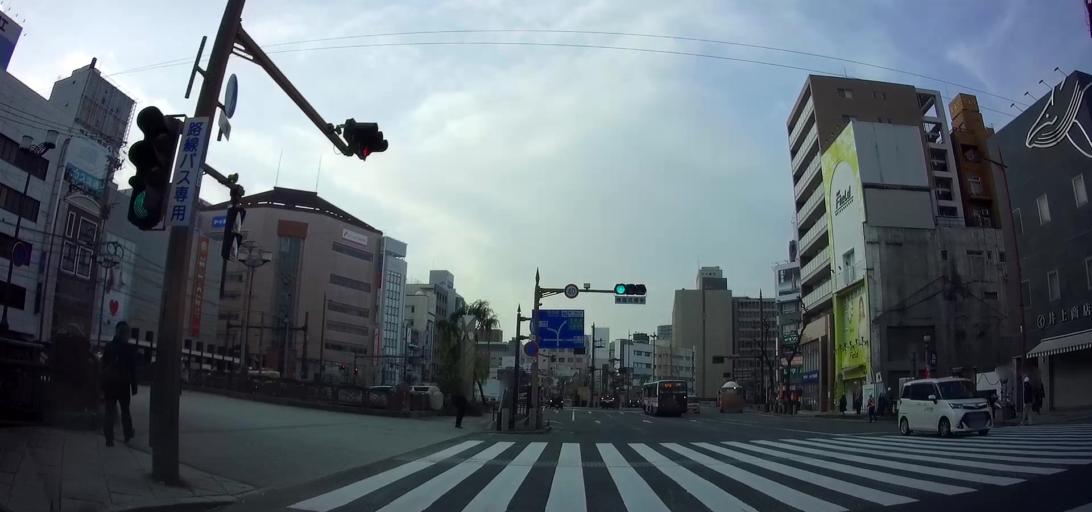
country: JP
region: Nagasaki
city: Nagasaki-shi
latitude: 32.7451
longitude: 129.8763
